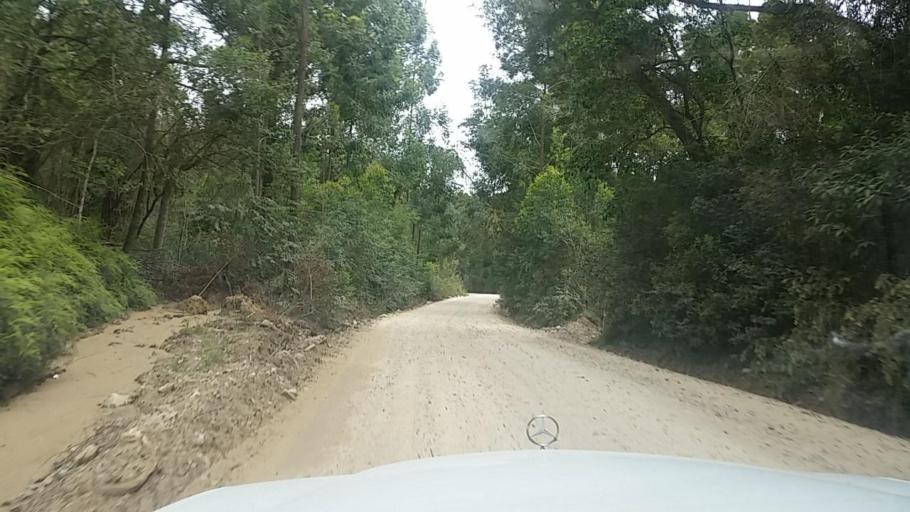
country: ZA
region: Western Cape
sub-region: Eden District Municipality
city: Knysna
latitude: -33.9961
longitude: 23.1162
